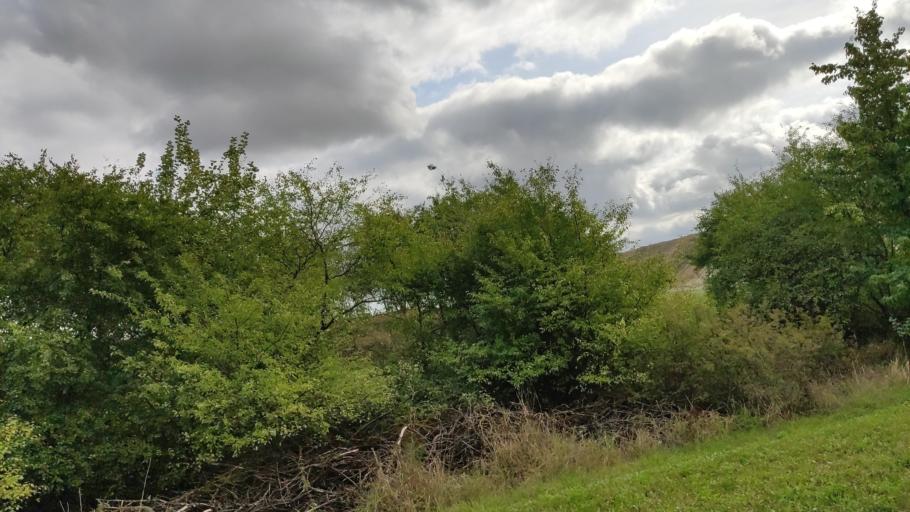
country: PL
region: Kujawsko-Pomorskie
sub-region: Powiat zninski
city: Barcin
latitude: 52.8375
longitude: 17.9510
